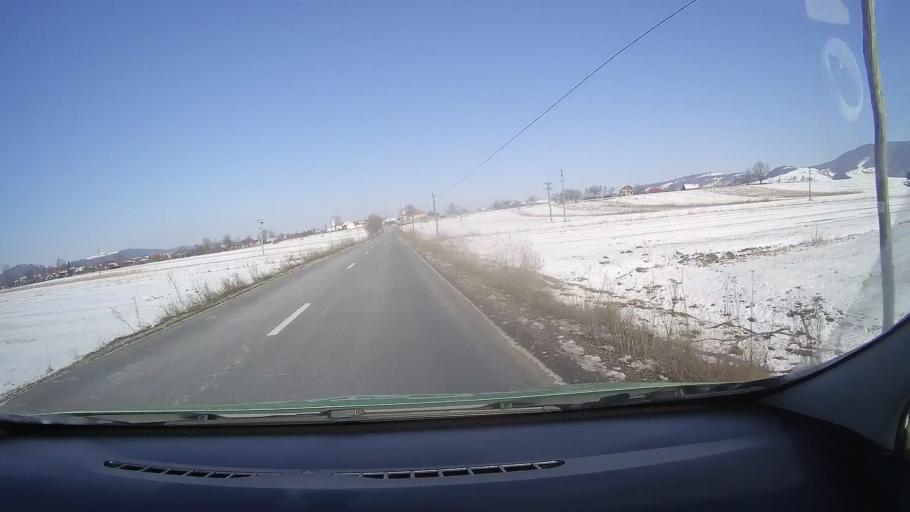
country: RO
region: Brasov
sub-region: Comuna Comana
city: Comana de Jos
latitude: 45.9080
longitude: 25.2292
